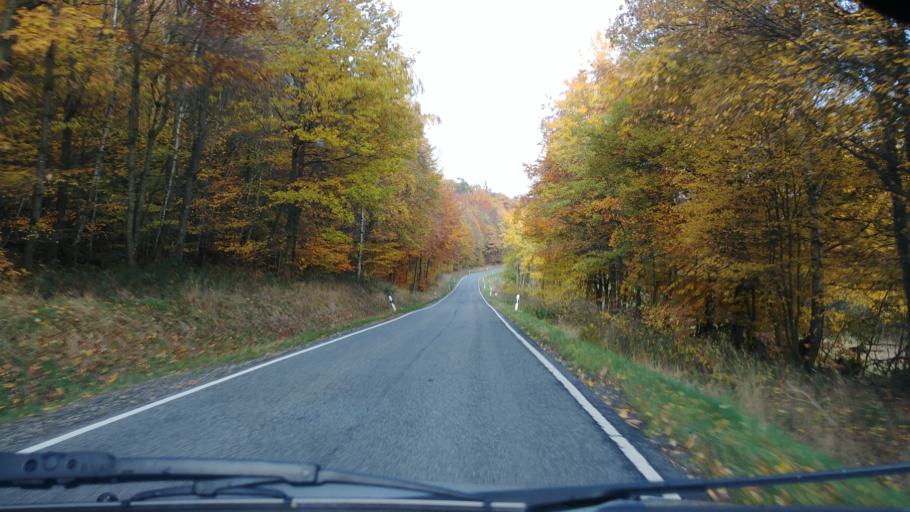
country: DE
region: Hesse
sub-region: Regierungsbezirk Darmstadt
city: Idstein
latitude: 50.2016
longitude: 8.2427
